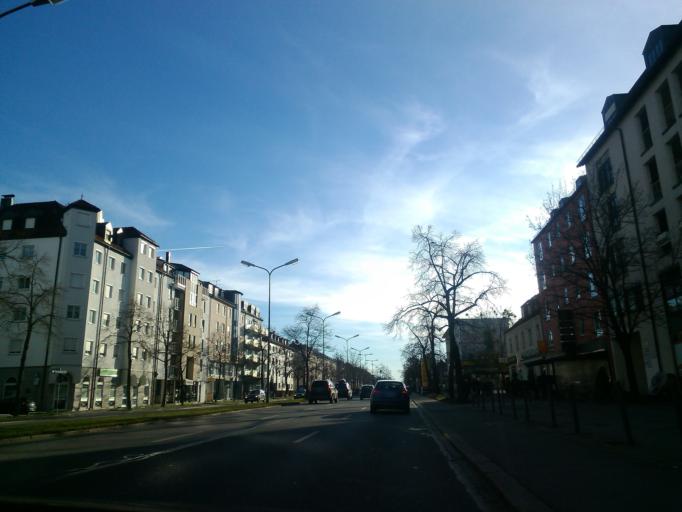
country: DE
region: Bavaria
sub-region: Upper Bavaria
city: Pasing
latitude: 48.1327
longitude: 11.5028
